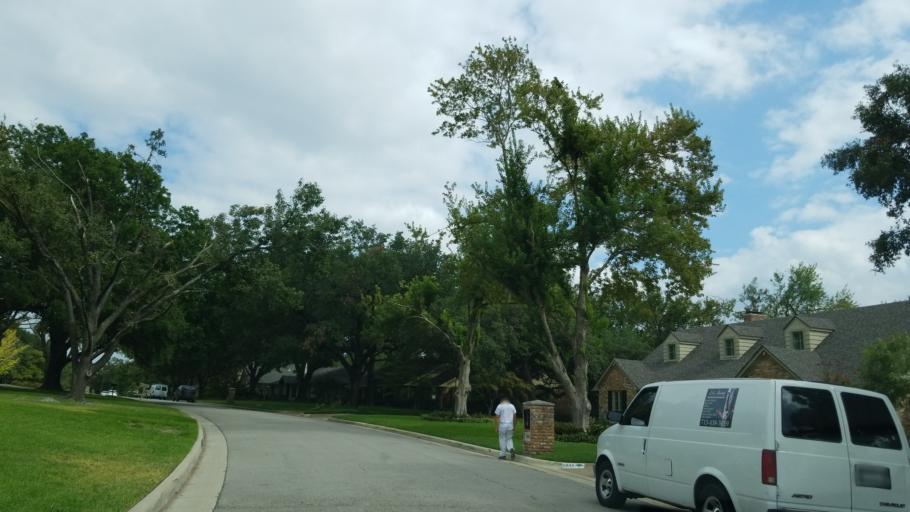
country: US
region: Texas
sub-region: Dallas County
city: Addison
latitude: 32.9421
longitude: -96.7848
